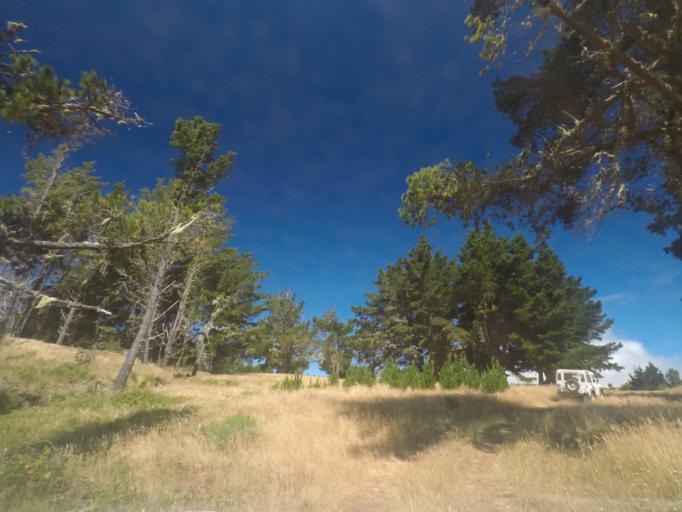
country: PT
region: Madeira
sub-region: Funchal
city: Nossa Senhora do Monte
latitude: 32.7113
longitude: -16.9070
